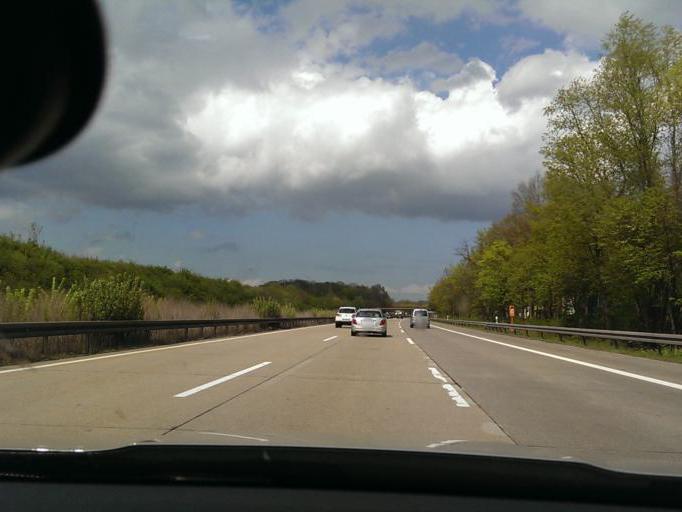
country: DE
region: Lower Saxony
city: Laatzen
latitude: 52.3314
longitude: 9.8637
